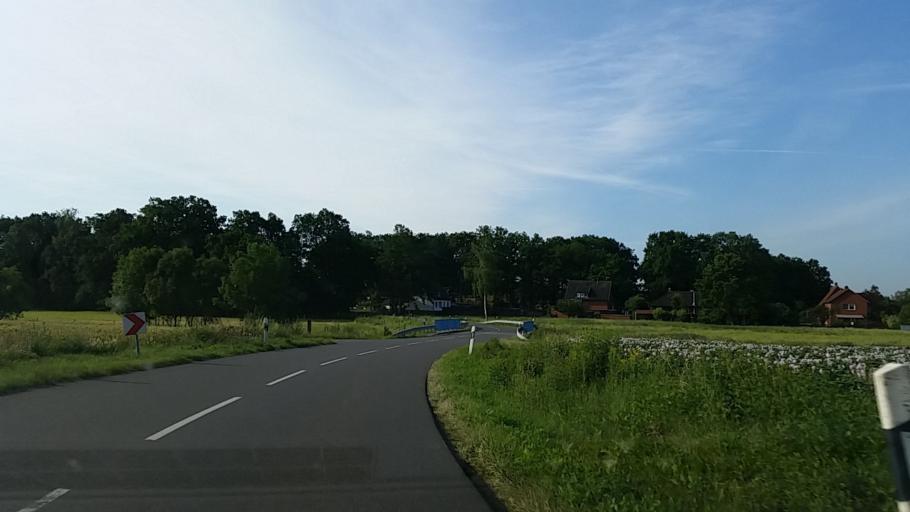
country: DE
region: Lower Saxony
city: Wieren
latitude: 52.9131
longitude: 10.6587
